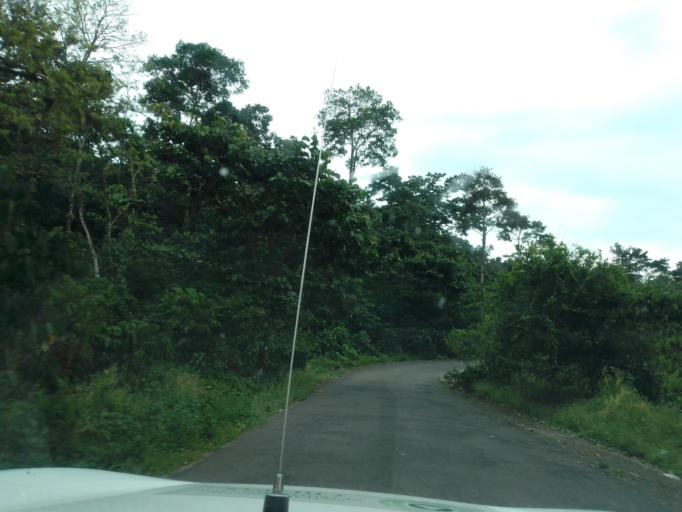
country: MX
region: Chiapas
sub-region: Union Juarez
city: Santo Domingo
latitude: 15.0508
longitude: -92.1207
